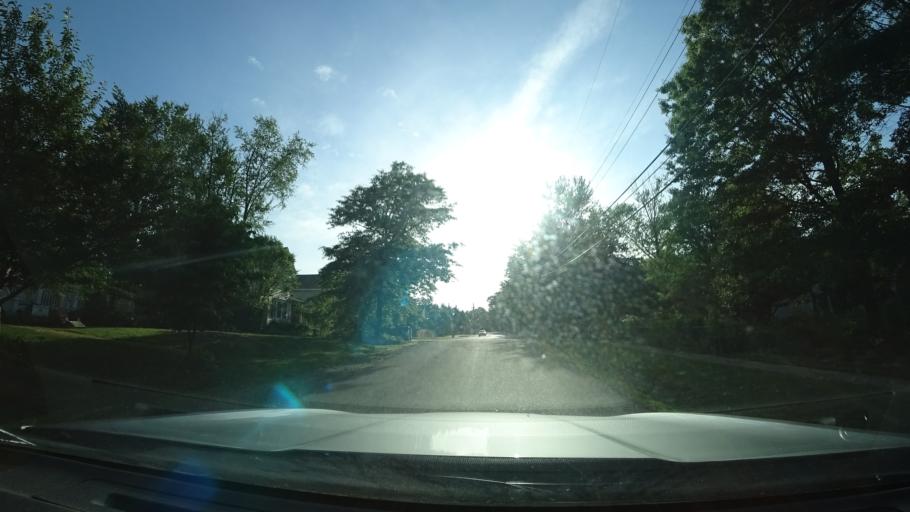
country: US
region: Virginia
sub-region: Fairfax County
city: Herndon
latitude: 38.9719
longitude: -77.3768
